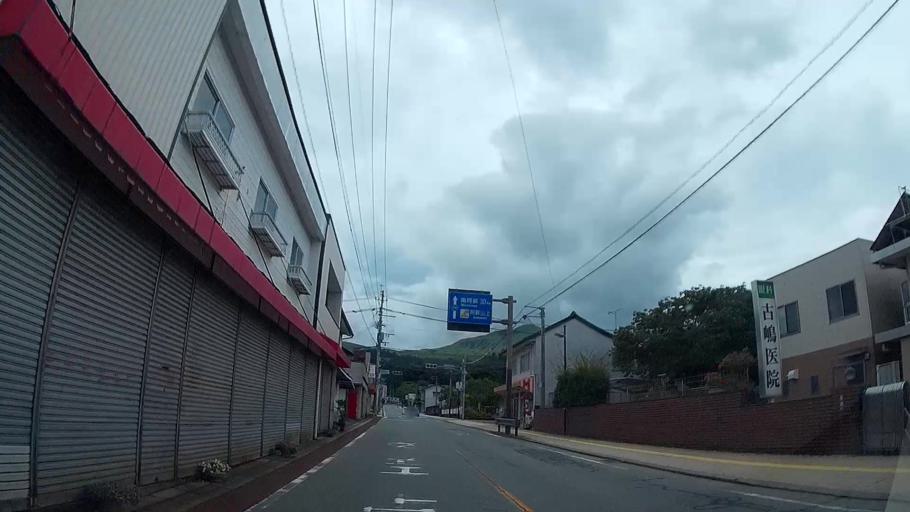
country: JP
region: Kumamoto
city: Aso
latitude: 32.9340
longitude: 131.0800
